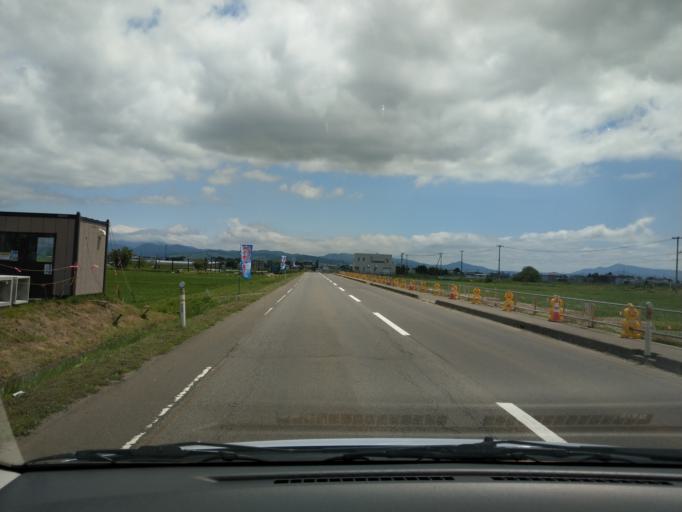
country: JP
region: Aomori
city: Kuroishi
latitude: 40.6570
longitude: 140.5640
